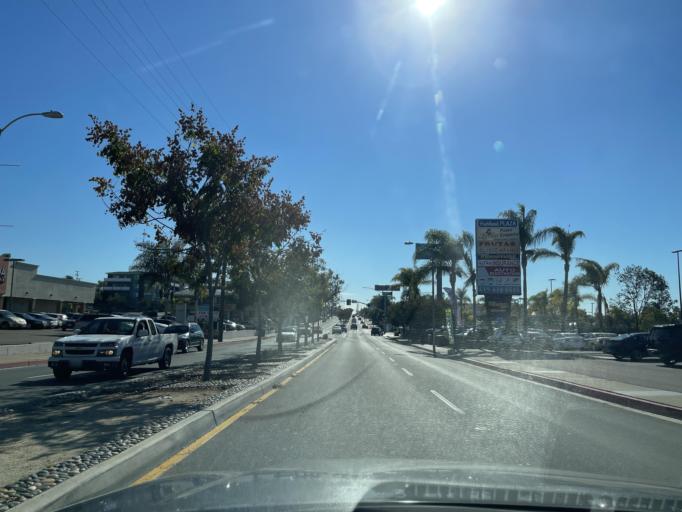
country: US
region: California
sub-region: San Diego County
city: National City
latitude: 32.6760
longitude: -117.0979
